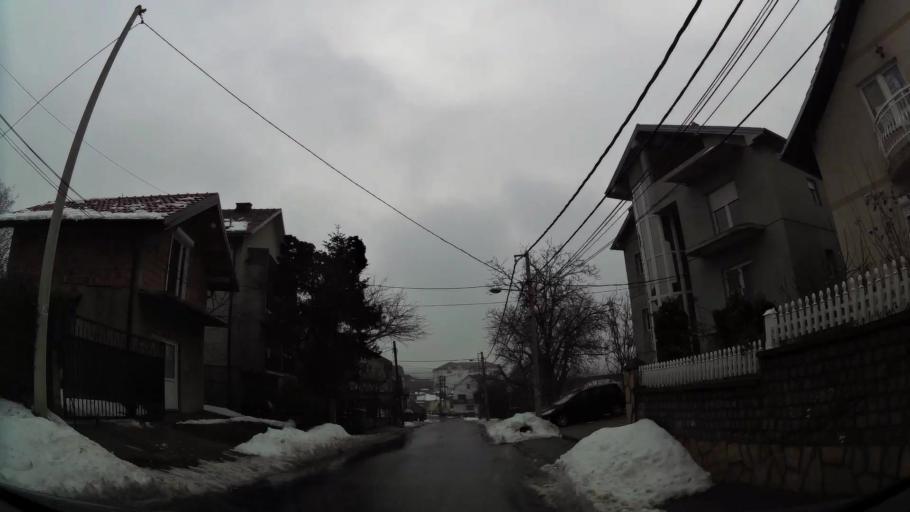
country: RS
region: Central Serbia
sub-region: Belgrade
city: Zvezdara
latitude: 44.7754
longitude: 20.5251
